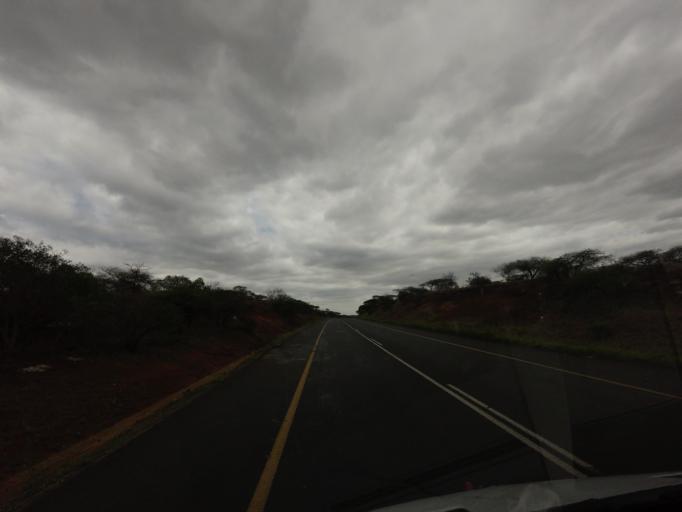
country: ZA
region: KwaZulu-Natal
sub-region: uMkhanyakude District Municipality
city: Hluhluwe
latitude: -27.8846
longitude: 32.1838
